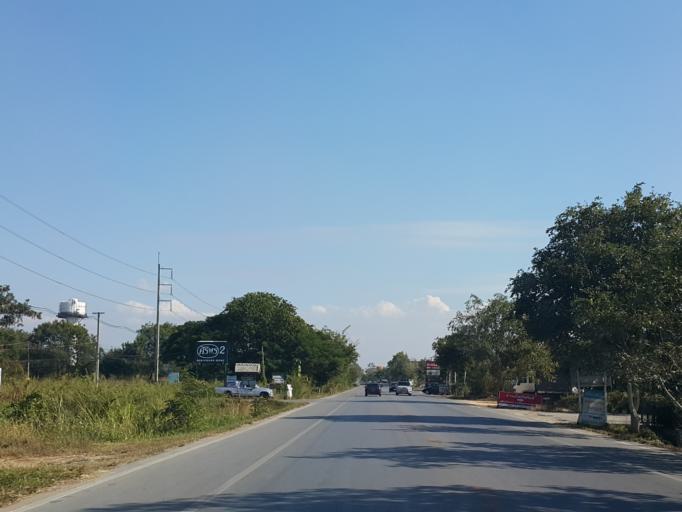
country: TH
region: Chiang Mai
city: San Sai
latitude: 18.8425
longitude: 99.0208
